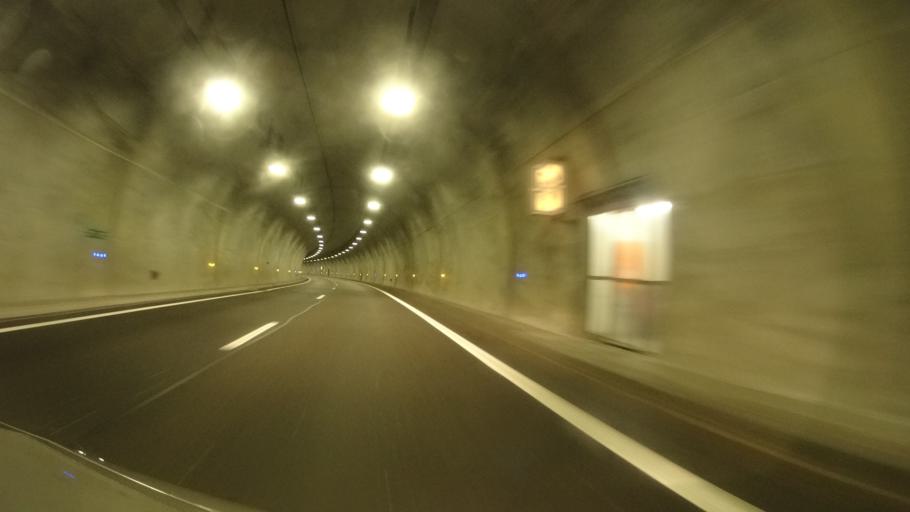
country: FR
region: Franche-Comte
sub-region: Departement du Doubs
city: Beure
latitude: 47.2129
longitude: 6.0251
